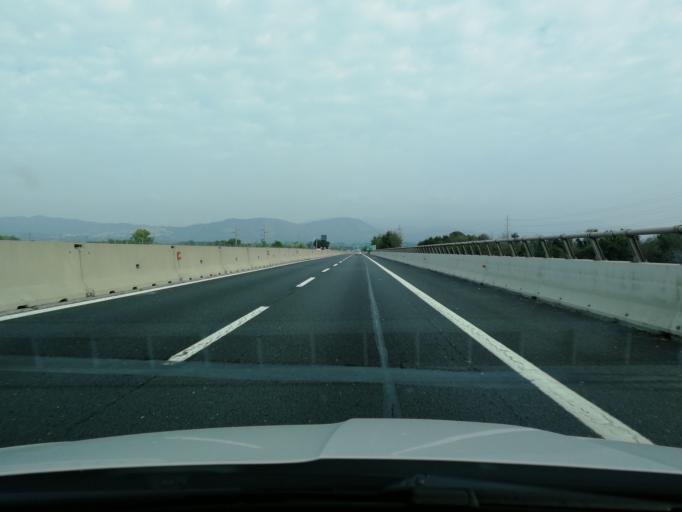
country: IT
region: Latium
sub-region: Citta metropolitana di Roma Capitale
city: Bagni di Tivoli
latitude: 41.9263
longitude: 12.7107
